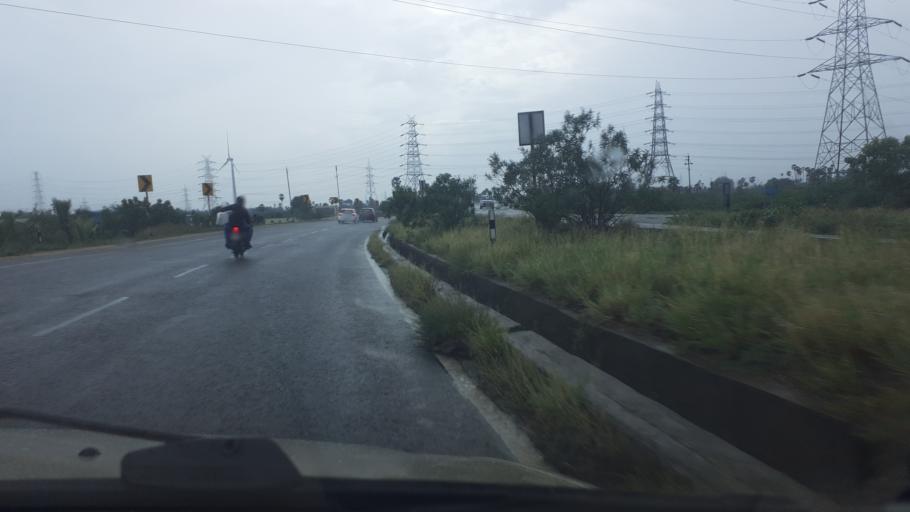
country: IN
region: Tamil Nadu
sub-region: Thoothukkudi
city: Kayattar
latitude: 8.9315
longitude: 77.7698
